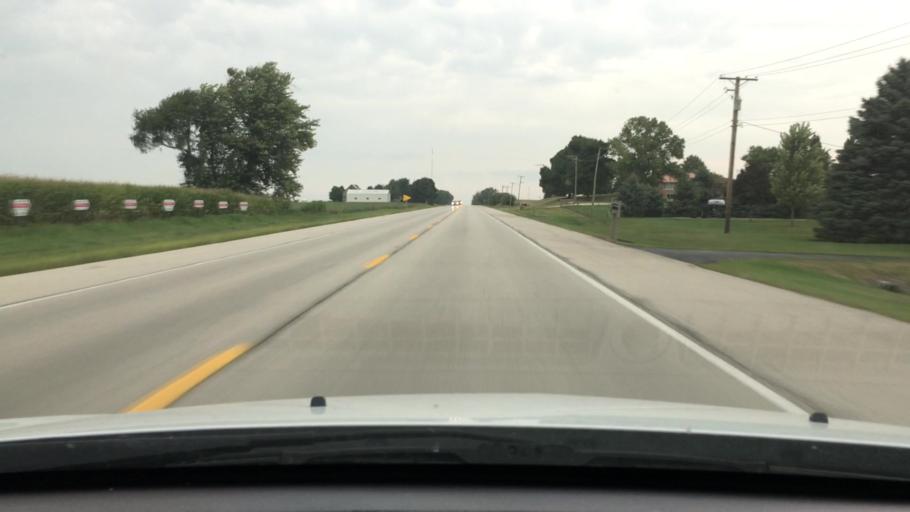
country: US
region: Illinois
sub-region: DeKalb County
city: DeKalb
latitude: 41.8556
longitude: -88.7539
